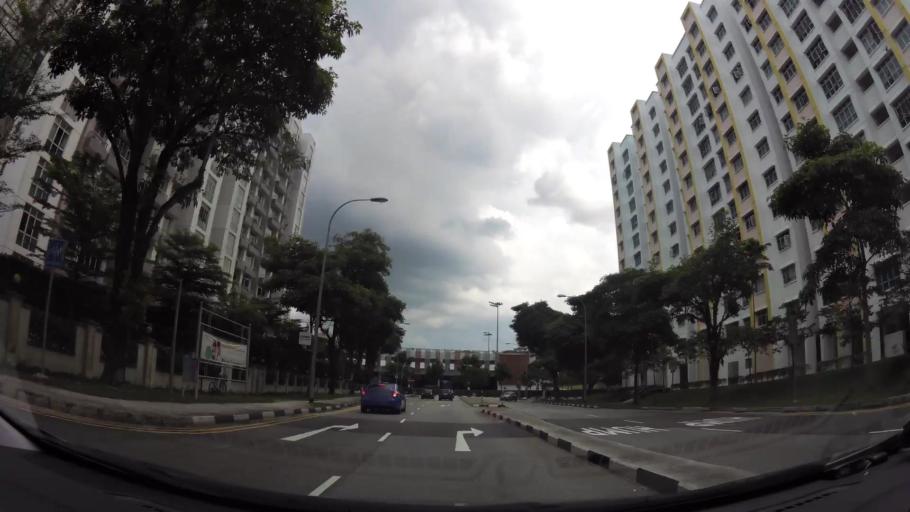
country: MY
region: Johor
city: Kampung Pasir Gudang Baru
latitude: 1.4236
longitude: 103.8489
